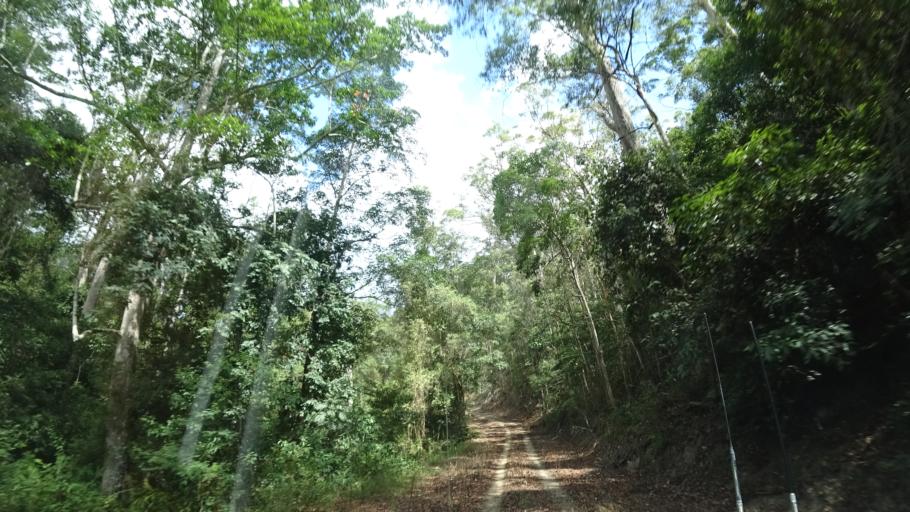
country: AU
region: Queensland
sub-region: Moreton Bay
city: Highvale
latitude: -27.3415
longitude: 152.7295
